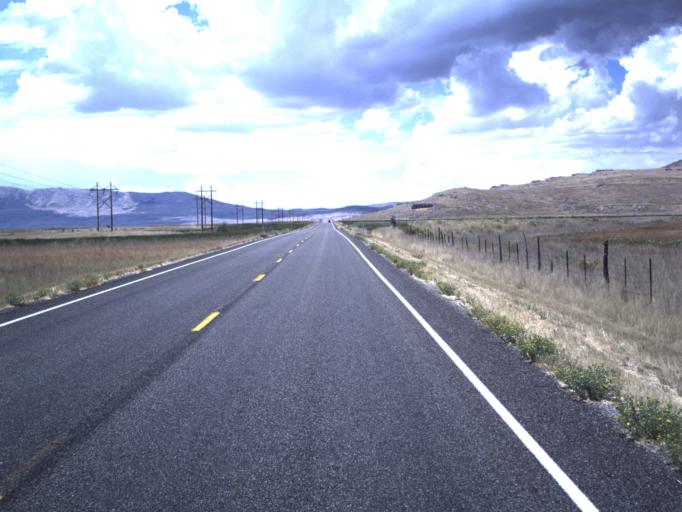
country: US
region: Utah
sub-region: Box Elder County
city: Tremonton
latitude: 41.6109
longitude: -112.3497
